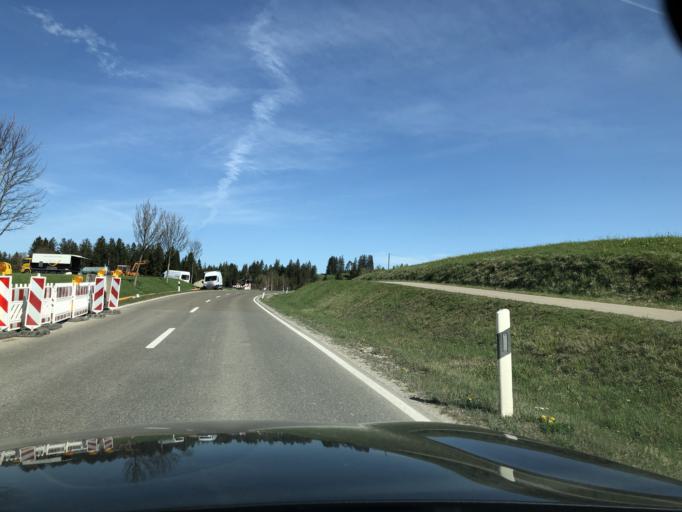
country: DE
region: Bavaria
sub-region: Swabia
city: Eisenberg
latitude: 47.6238
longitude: 10.6066
